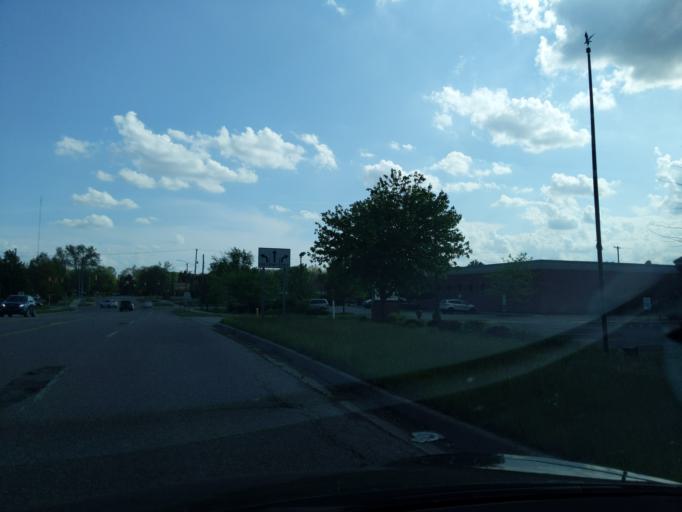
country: US
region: Michigan
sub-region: Ingham County
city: Okemos
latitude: 42.7190
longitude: -84.4093
